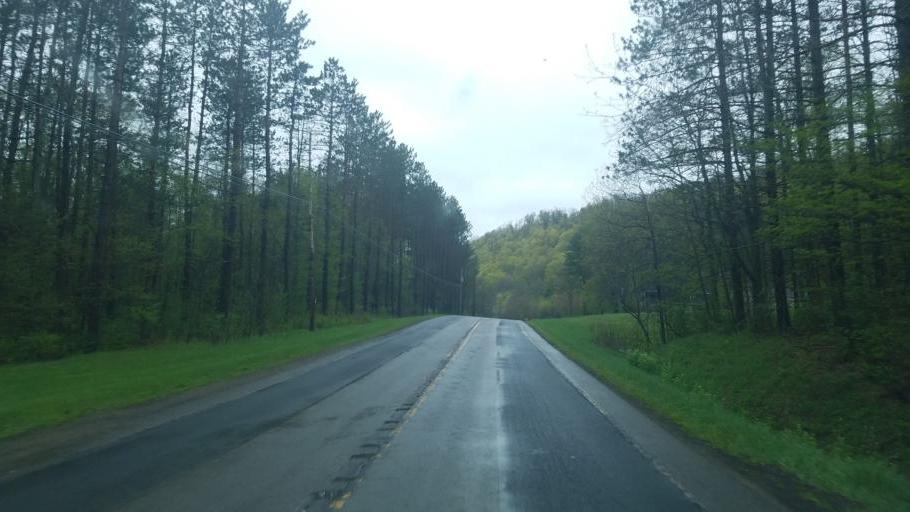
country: US
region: Pennsylvania
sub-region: Potter County
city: Coudersport
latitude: 41.8232
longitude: -77.9756
